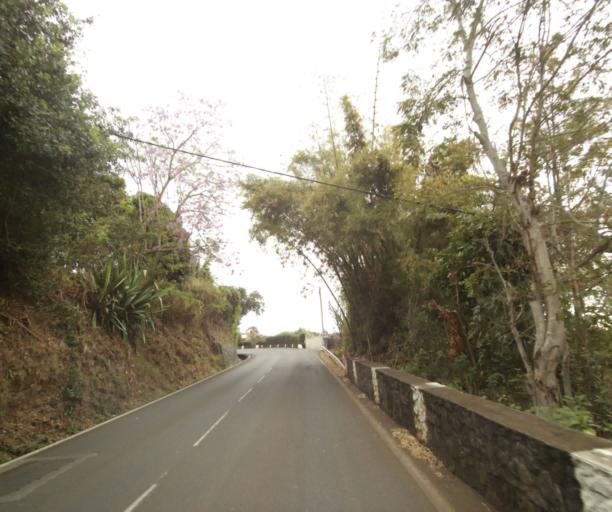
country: RE
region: Reunion
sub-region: Reunion
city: Saint-Paul
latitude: -21.0452
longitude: 55.2881
